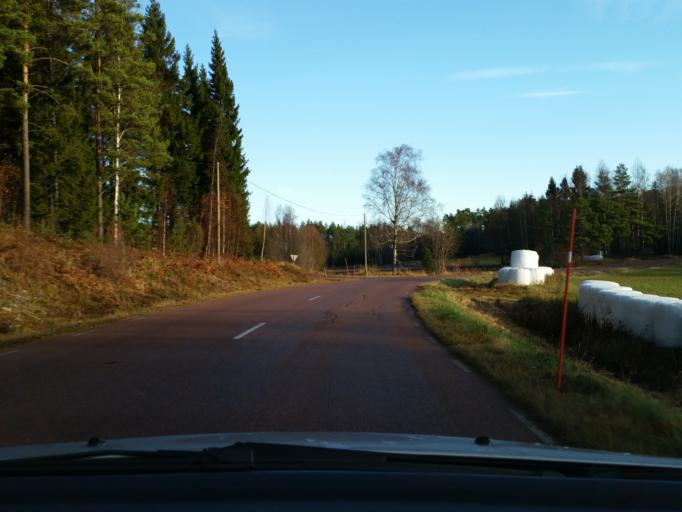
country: AX
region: Alands landsbygd
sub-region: Sund
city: Sund
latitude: 60.3084
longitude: 20.1601
